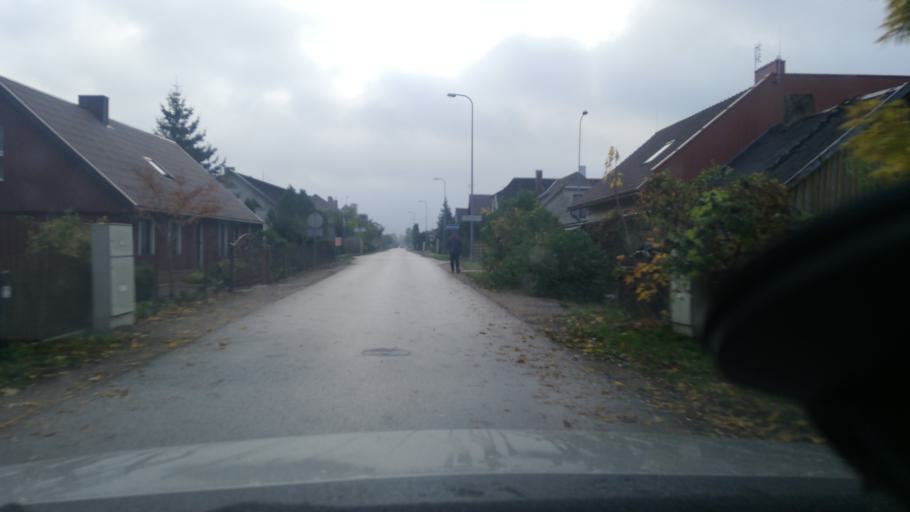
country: LT
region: Klaipedos apskritis
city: Kretinga
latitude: 55.8846
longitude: 21.2502
